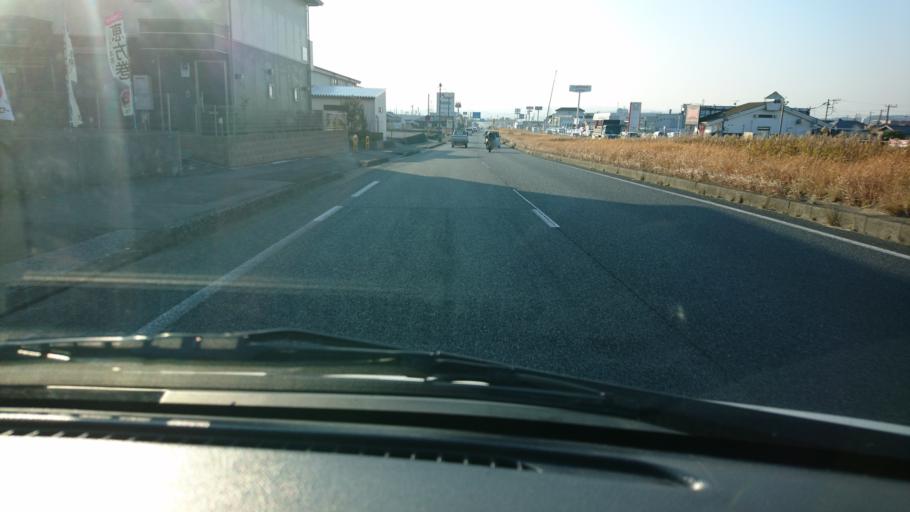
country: JP
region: Chiba
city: Kimitsu
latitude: 35.3322
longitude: 139.9233
